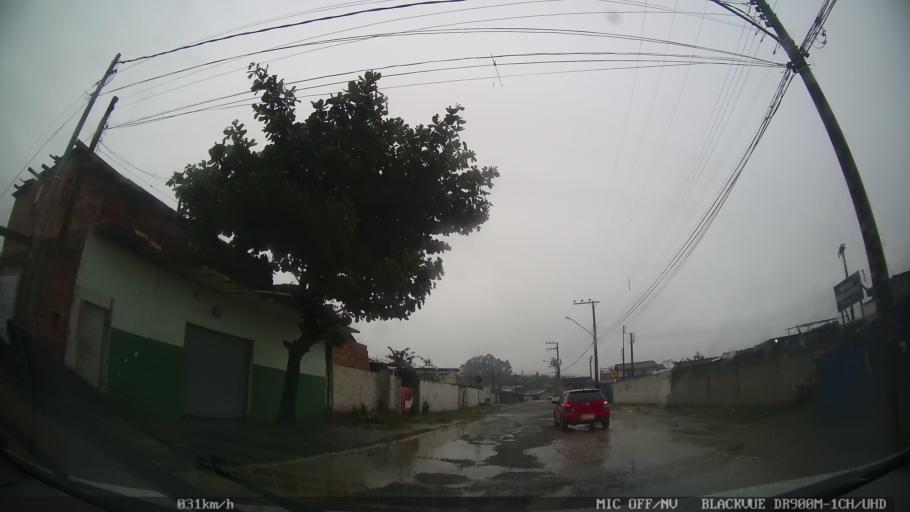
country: BR
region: Santa Catarina
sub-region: Itajai
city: Itajai
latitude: -26.9194
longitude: -48.6902
